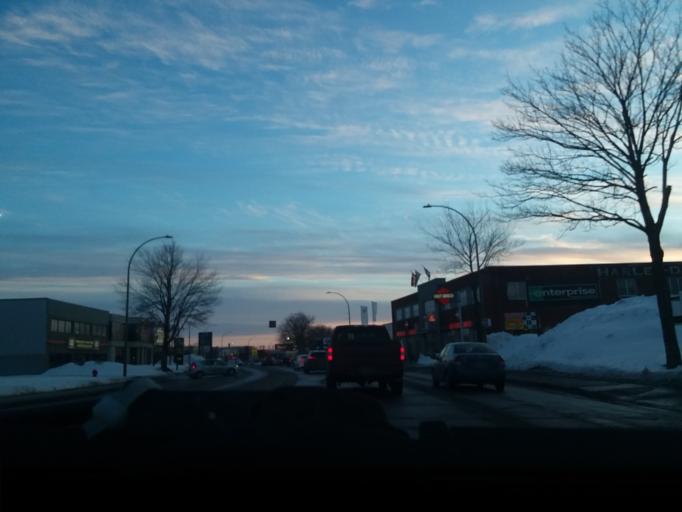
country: CA
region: Quebec
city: Saint-Raymond
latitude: 45.4604
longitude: -73.6262
